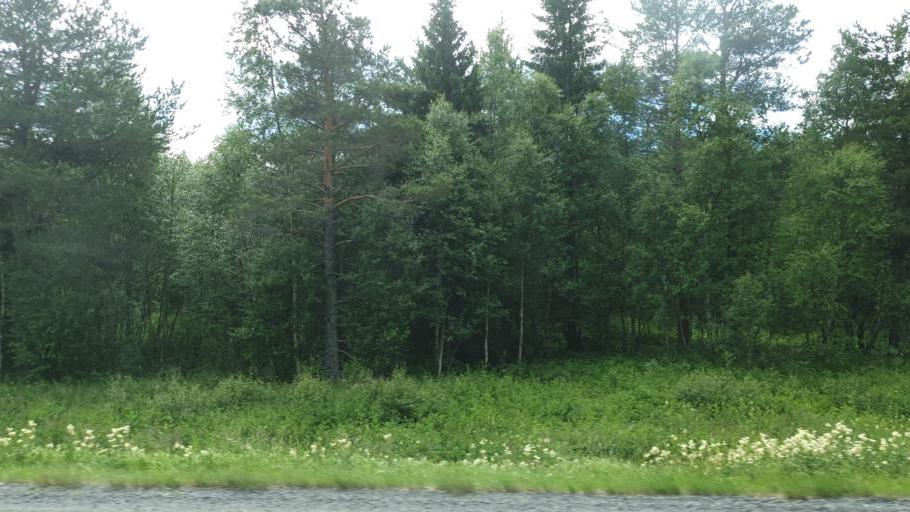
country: NO
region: Sor-Trondelag
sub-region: Rennebu
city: Berkak
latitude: 62.8700
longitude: 10.0481
